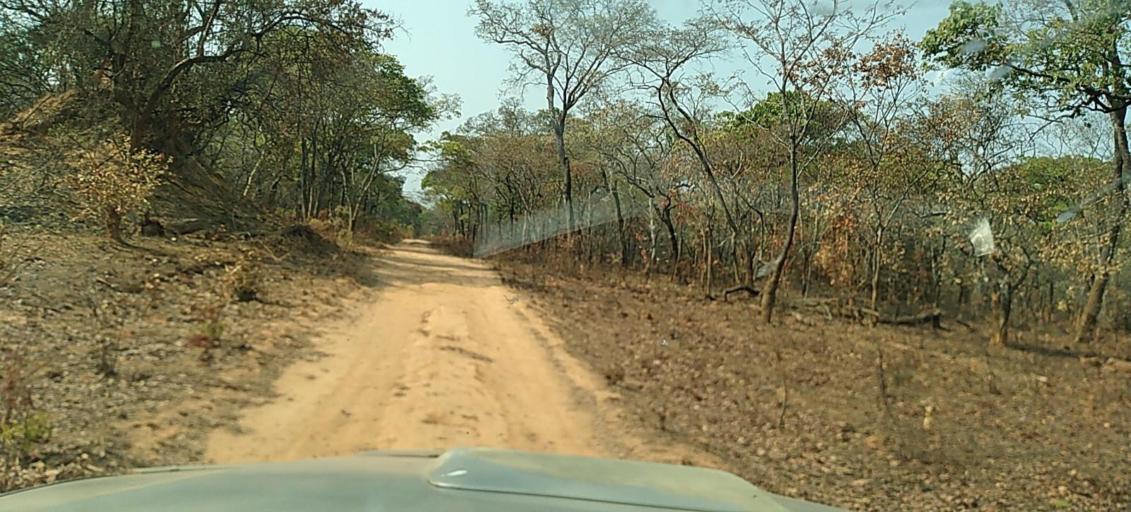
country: ZM
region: North-Western
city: Kasempa
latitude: -13.5282
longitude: 26.4095
